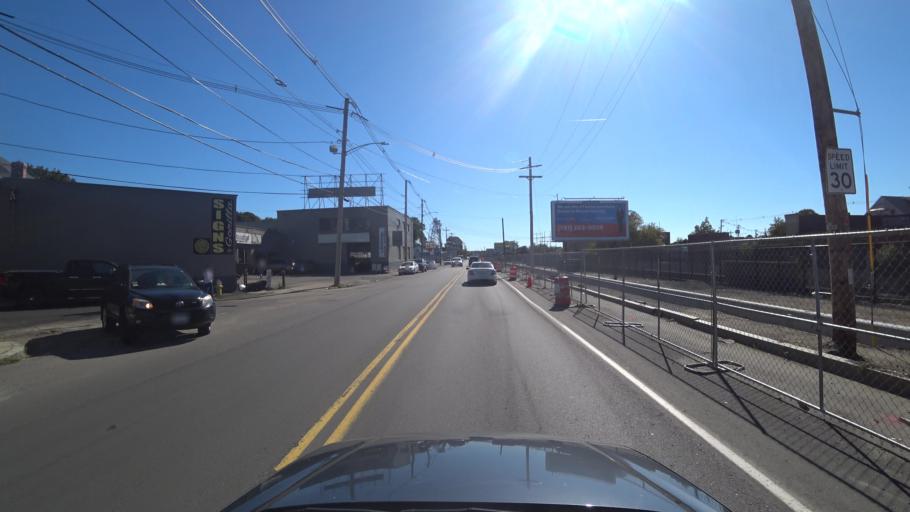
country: US
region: Massachusetts
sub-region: Essex County
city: Salem
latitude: 42.5171
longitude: -70.8957
